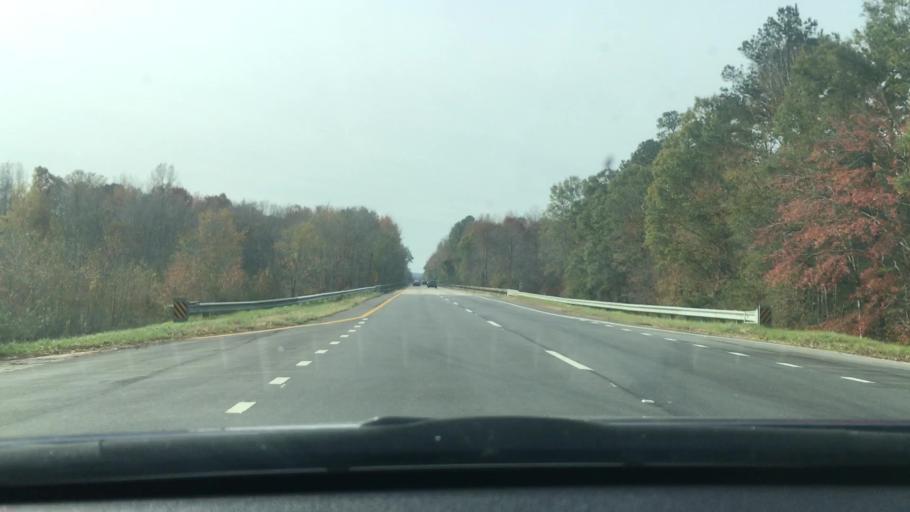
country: US
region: South Carolina
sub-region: Sumter County
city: Stateburg
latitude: 33.9528
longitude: -80.5756
